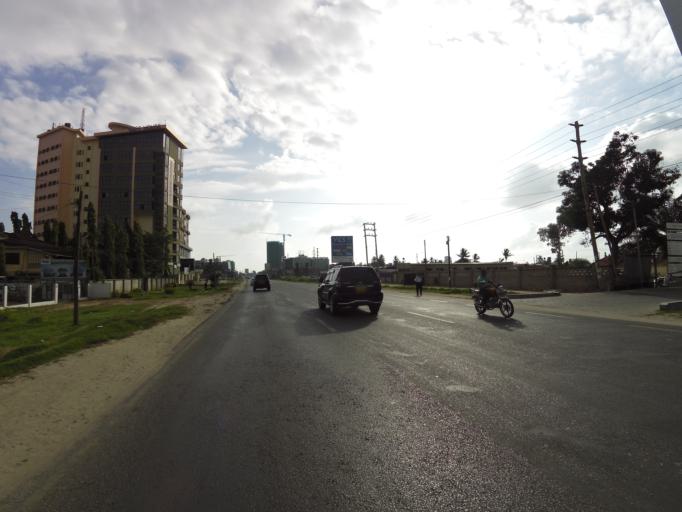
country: TZ
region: Dar es Salaam
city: Magomeni
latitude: -6.7785
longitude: 39.2547
